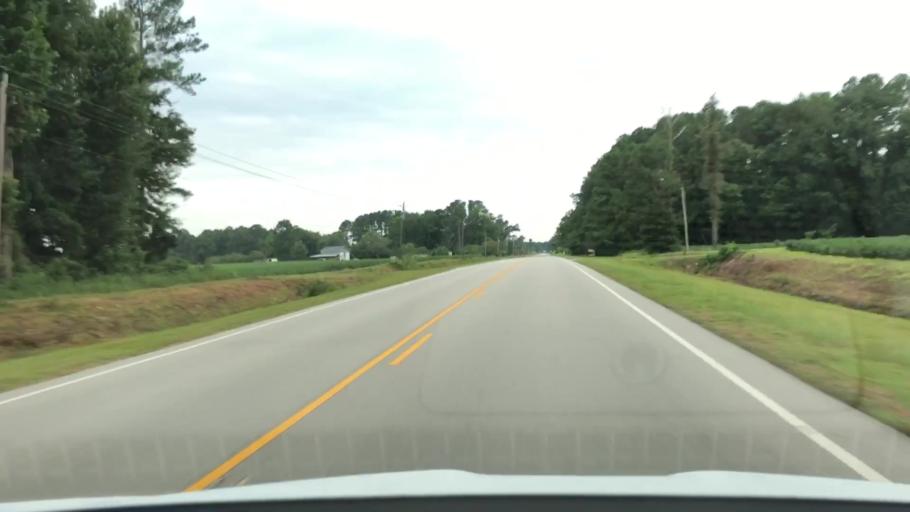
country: US
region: North Carolina
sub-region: Jones County
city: Trenton
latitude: 35.0334
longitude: -77.3212
